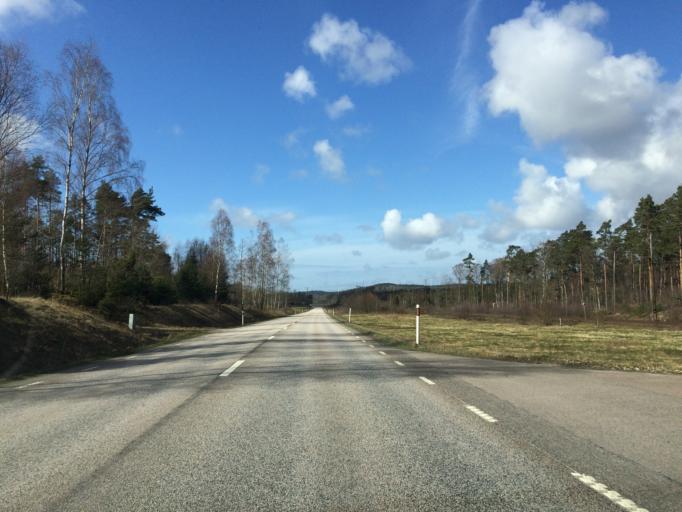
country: SE
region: Halland
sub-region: Laholms Kommun
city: Knared
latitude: 56.5052
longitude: 13.3500
